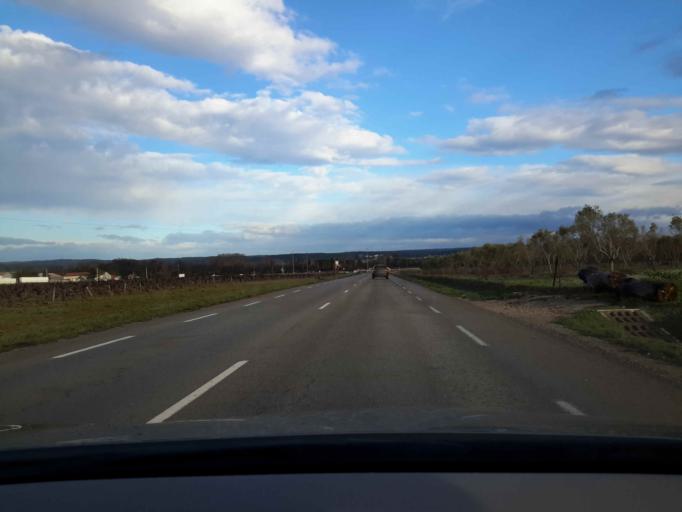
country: FR
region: Languedoc-Roussillon
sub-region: Departement du Gard
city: Aubord
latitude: 43.7665
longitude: 4.3297
